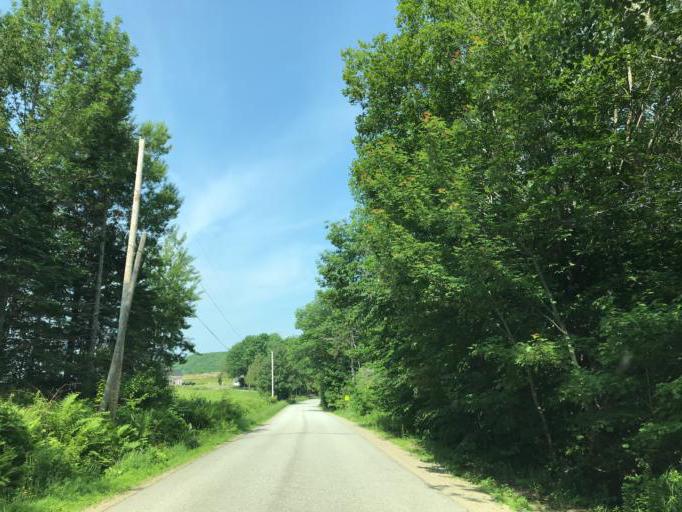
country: US
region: Maine
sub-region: Knox County
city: Hope
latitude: 44.2296
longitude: -69.1599
